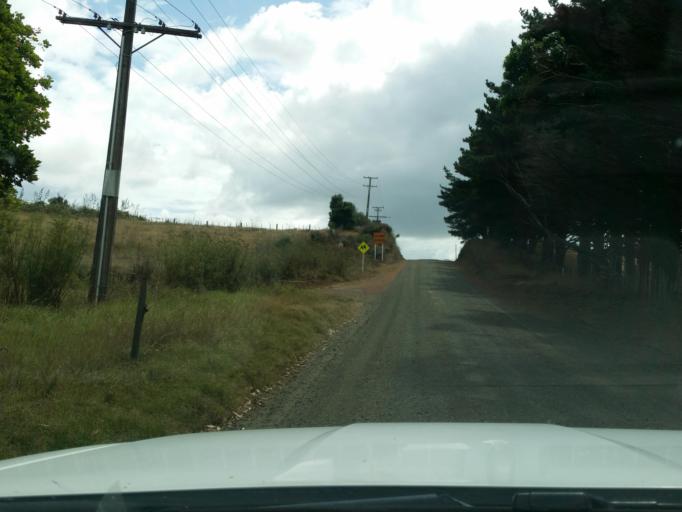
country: NZ
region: Auckland
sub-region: Auckland
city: Wellsford
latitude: -36.3544
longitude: 174.1741
